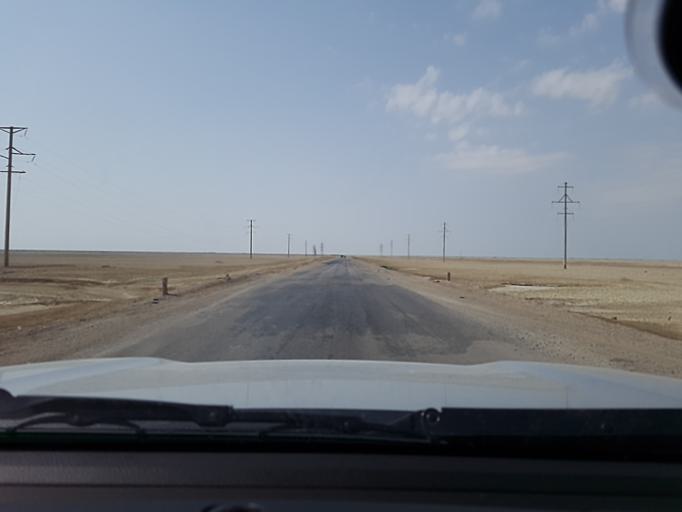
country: TM
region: Balkan
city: Gumdag
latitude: 39.0609
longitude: 54.5843
